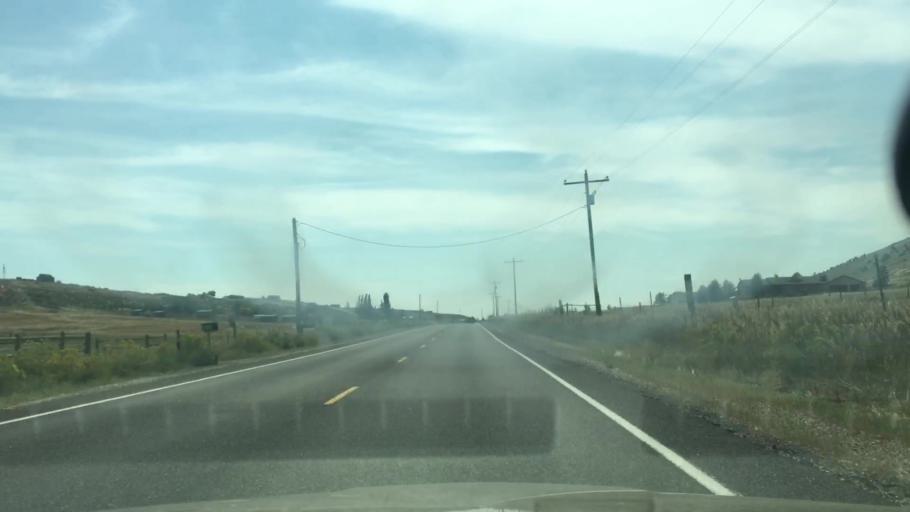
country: US
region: Colorado
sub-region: Larimer County
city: Campion
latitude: 40.3570
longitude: -105.1853
